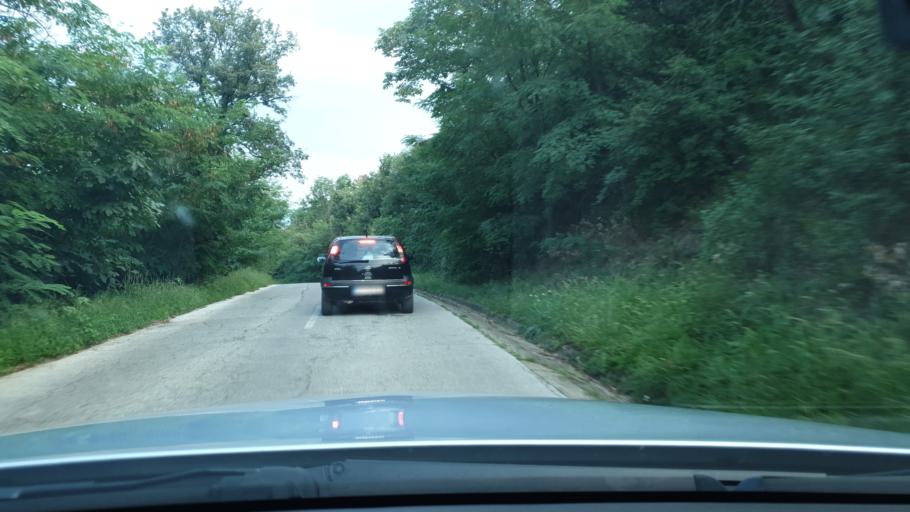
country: RS
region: Autonomna Pokrajina Vojvodina
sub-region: Juznobanatski Okrug
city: Vrsac
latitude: 45.1232
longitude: 21.3286
